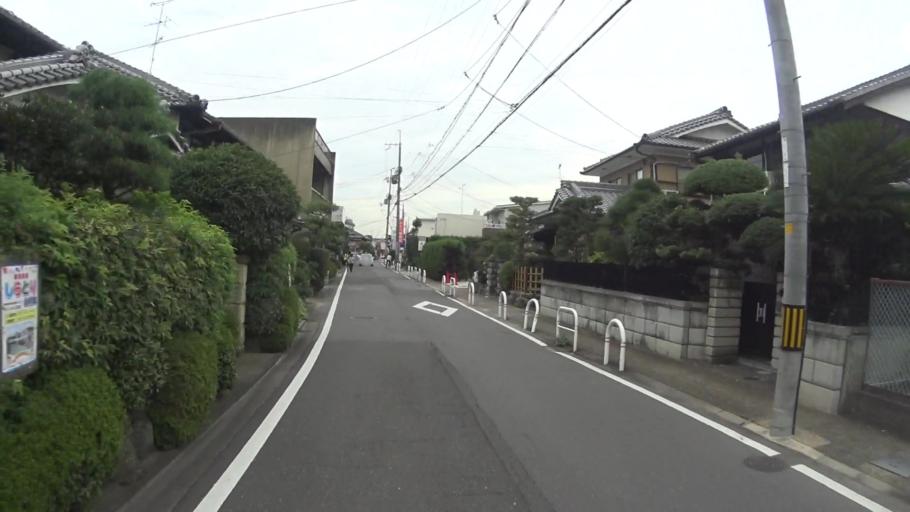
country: JP
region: Kyoto
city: Tanabe
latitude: 34.8538
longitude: 135.7768
